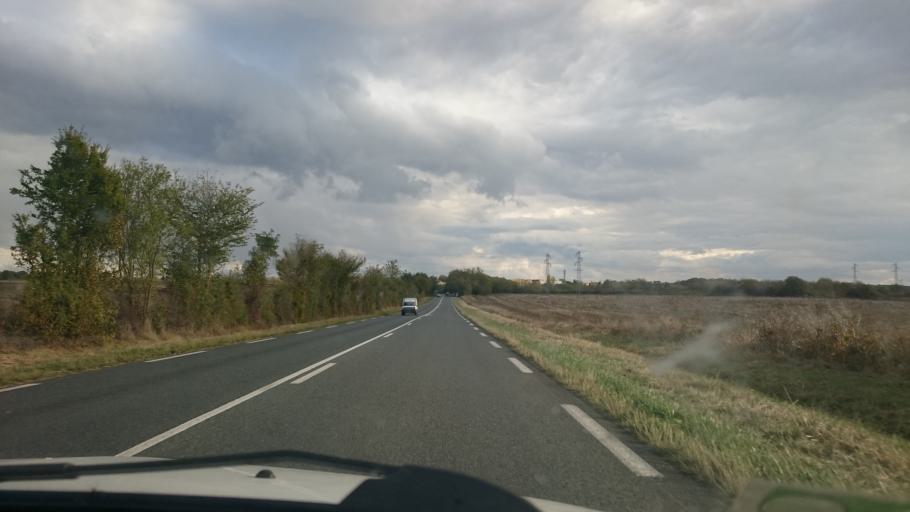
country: FR
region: Centre
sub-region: Departement de l'Indre
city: Saint-Marcel
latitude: 46.6142
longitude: 1.4996
